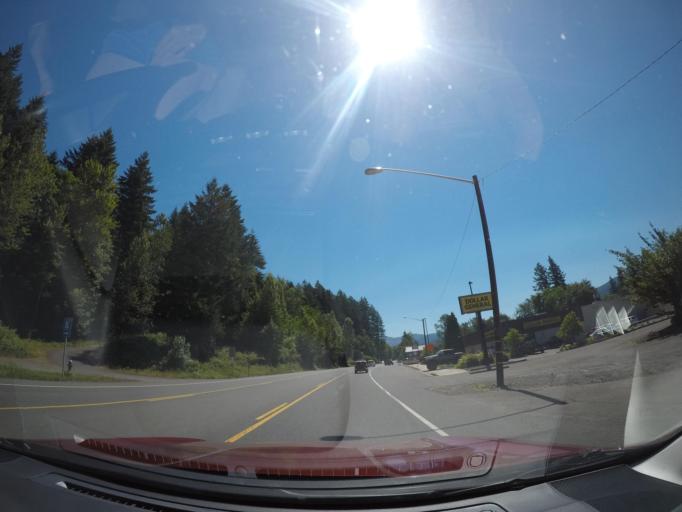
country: US
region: Oregon
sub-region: Linn County
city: Mill City
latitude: 44.7570
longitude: -122.4800
